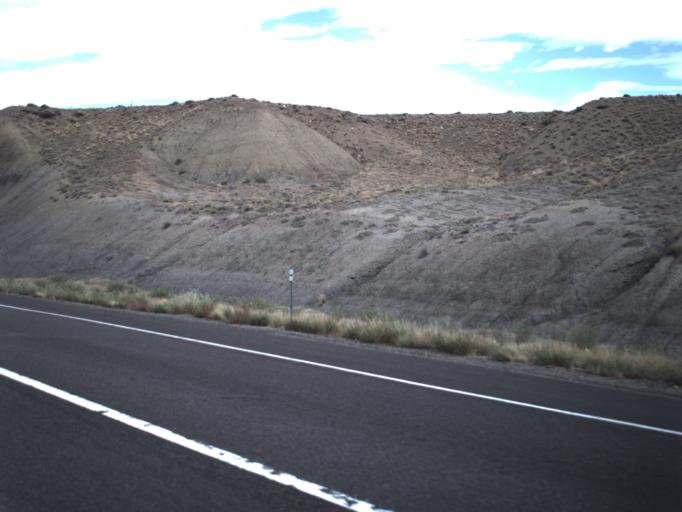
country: US
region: Utah
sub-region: Grand County
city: Moab
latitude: 38.9400
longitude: -109.8285
